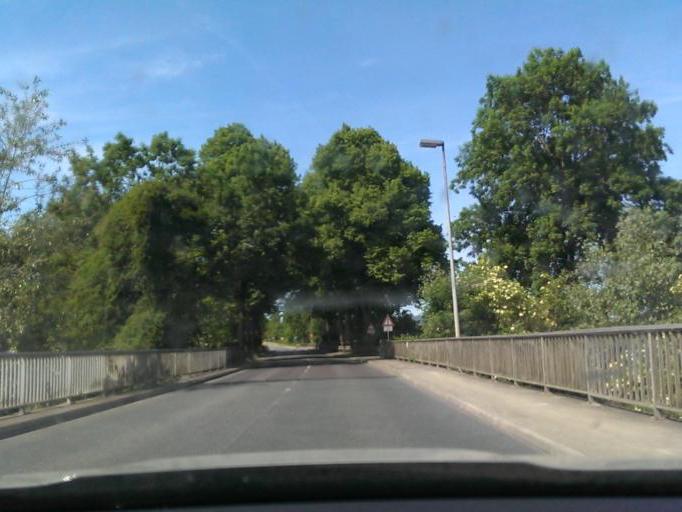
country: DE
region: Lower Saxony
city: Nordstemmen
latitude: 52.1473
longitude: 9.7679
